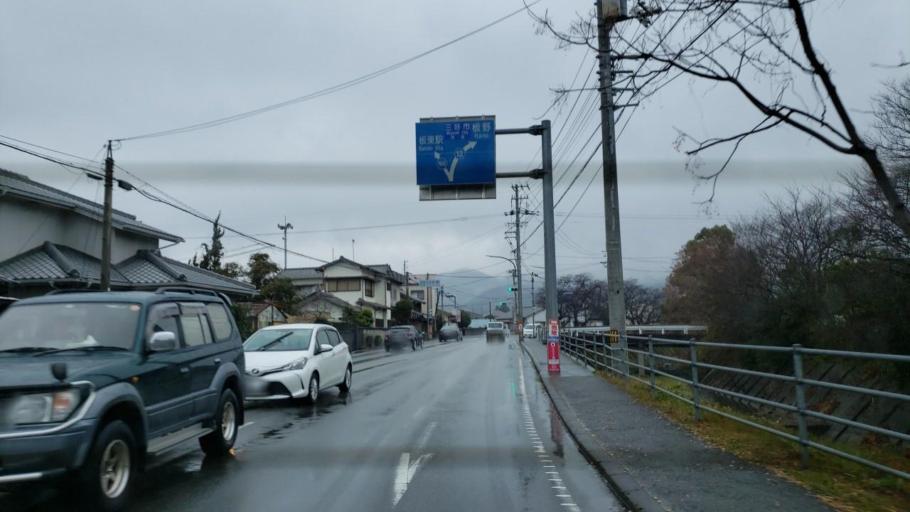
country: JP
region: Tokushima
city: Tokushima-shi
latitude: 34.1561
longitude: 134.5104
